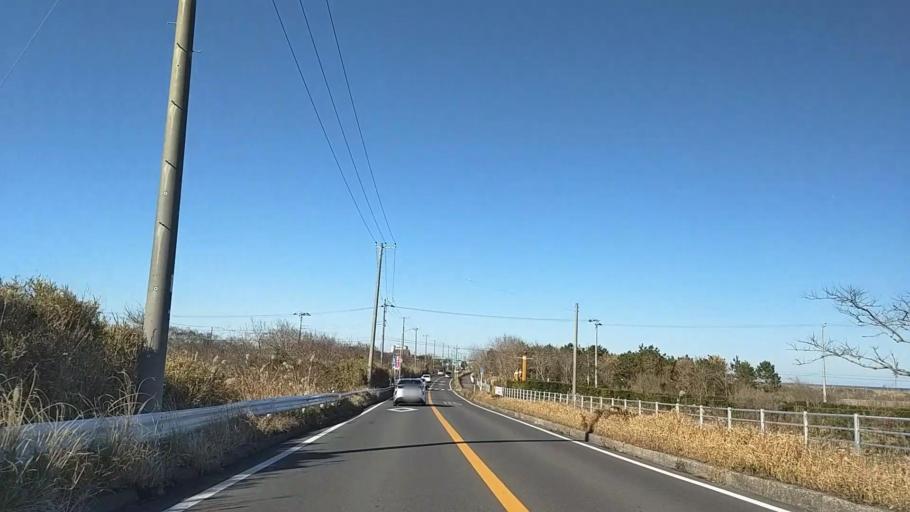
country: JP
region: Chiba
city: Ohara
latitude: 35.3346
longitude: 140.3920
